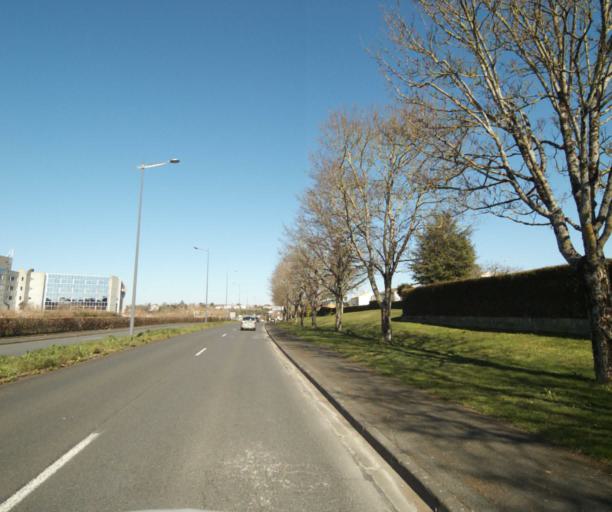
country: FR
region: Poitou-Charentes
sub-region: Departement des Deux-Sevres
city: Niort
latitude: 46.3292
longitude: -0.4845
